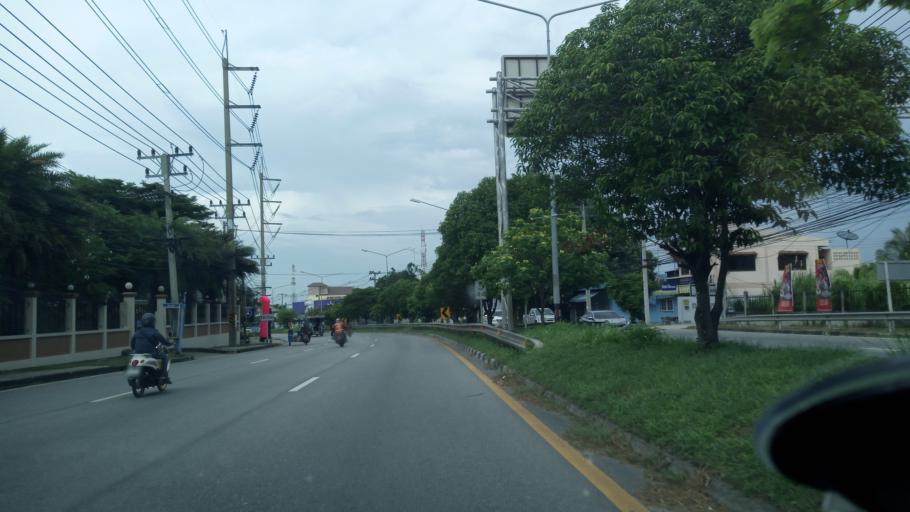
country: TH
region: Chon Buri
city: Chon Buri
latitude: 13.3885
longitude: 101.0174
